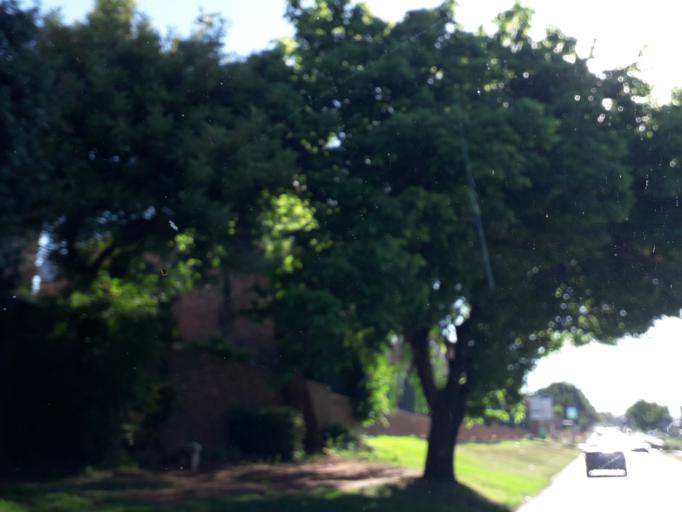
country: ZA
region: Gauteng
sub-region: City of Johannesburg Metropolitan Municipality
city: Roodepoort
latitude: -26.1513
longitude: 27.9425
